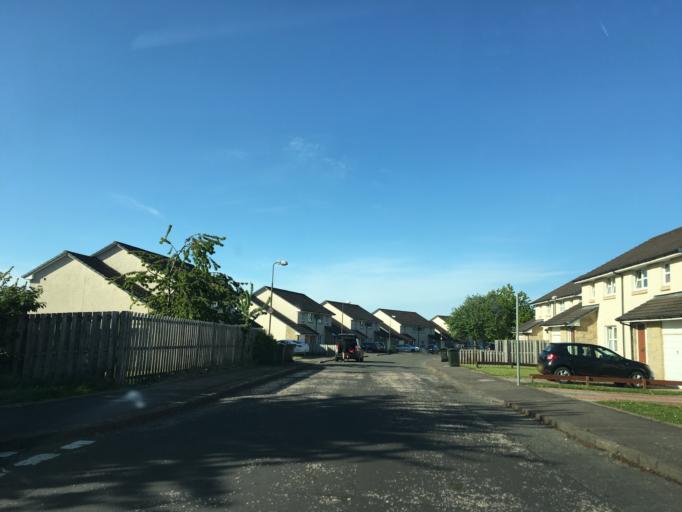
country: GB
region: Scotland
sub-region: Edinburgh
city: Colinton
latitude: 55.9216
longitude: -3.2579
